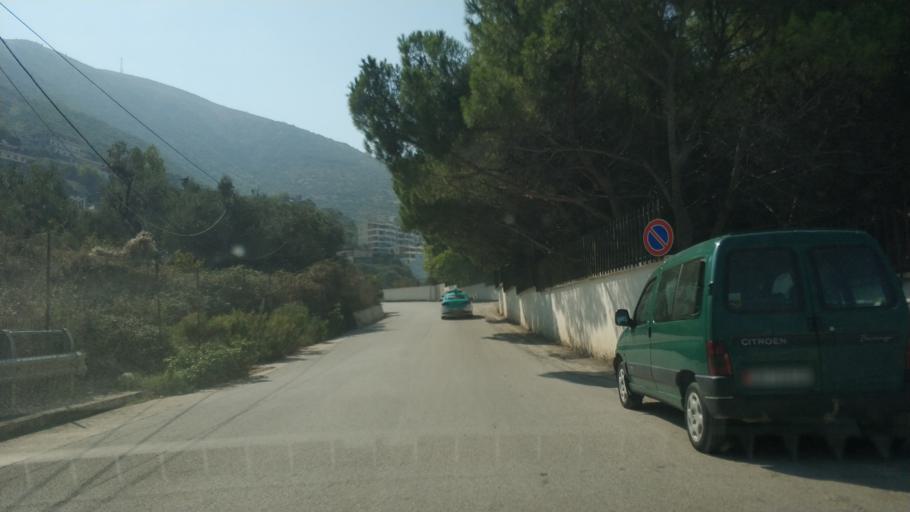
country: AL
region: Vlore
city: Vlore
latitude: 40.4195
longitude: 19.4866
